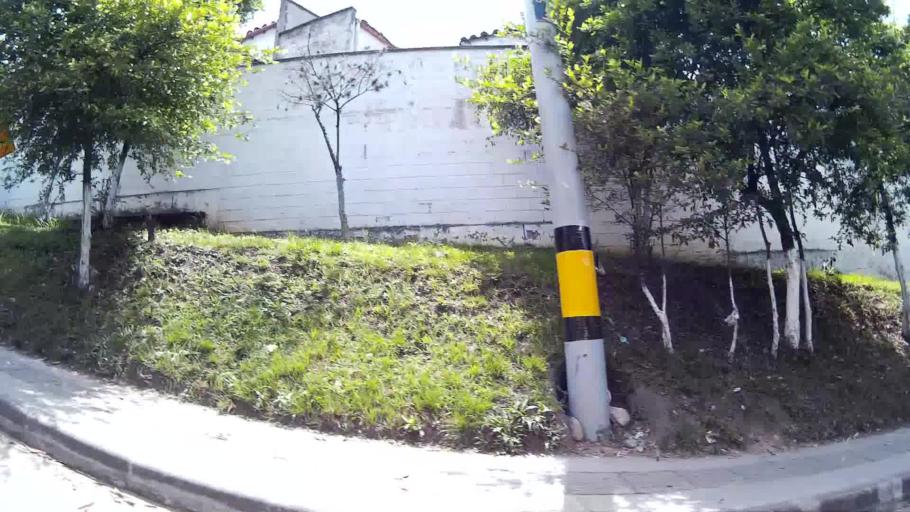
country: CO
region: Antioquia
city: Medellin
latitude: 6.2581
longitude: -75.6278
